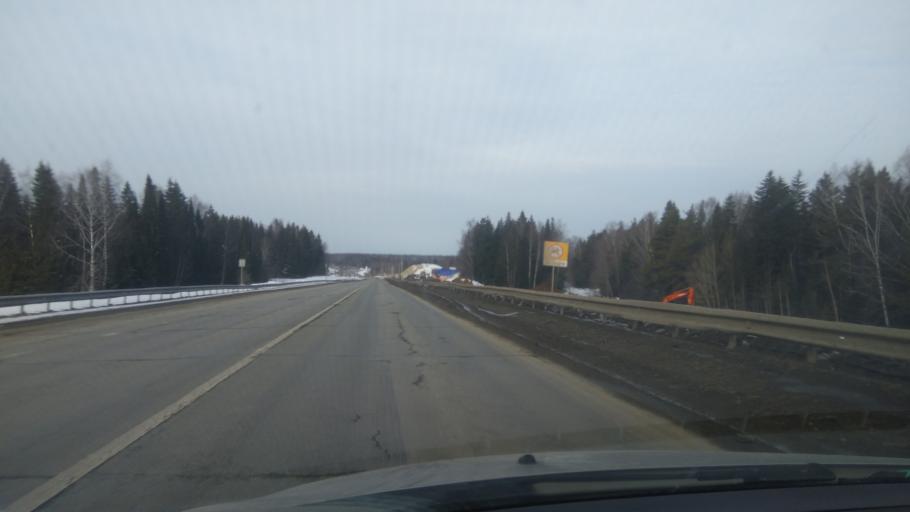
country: RU
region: Sverdlovsk
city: Bisert'
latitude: 56.8294
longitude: 59.0538
